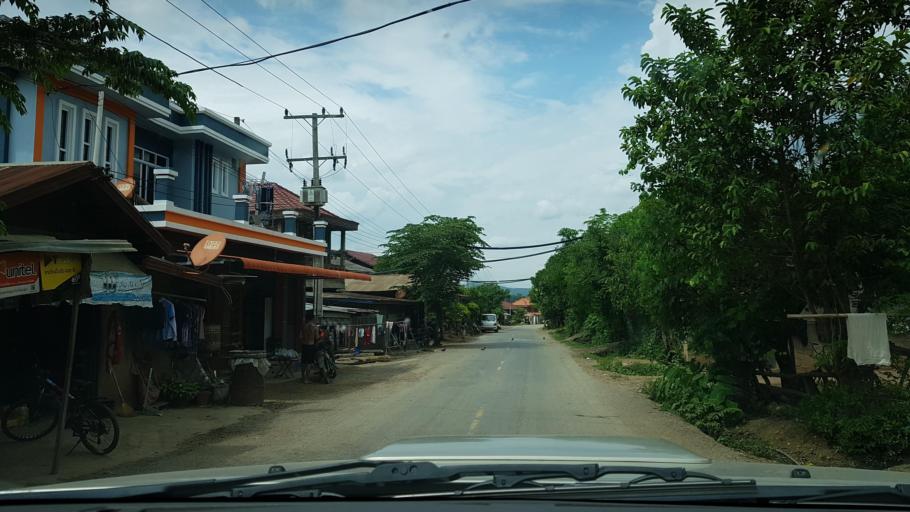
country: LA
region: Loungnamtha
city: Muang Nale
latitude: 20.2526
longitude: 101.5850
